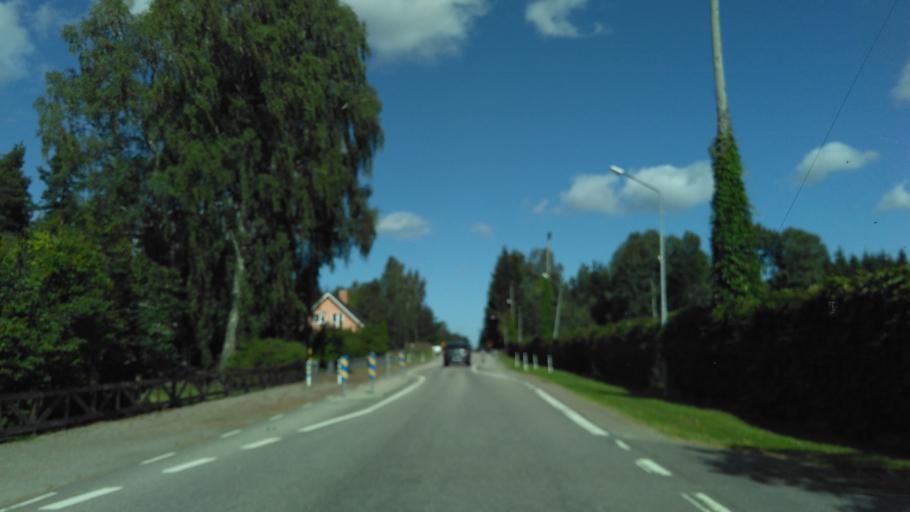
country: SE
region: Vaestra Goetaland
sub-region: Vara Kommun
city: Vara
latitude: 58.1768
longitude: 13.0014
